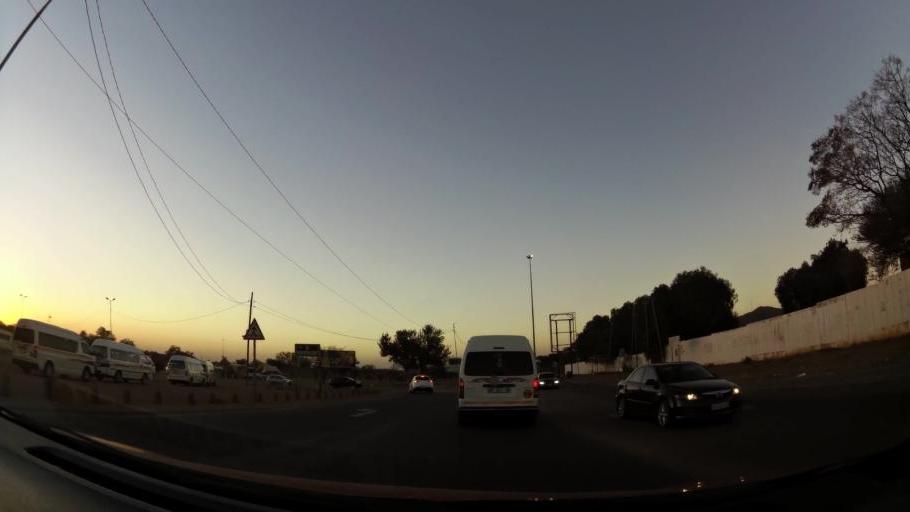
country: ZA
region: North-West
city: Ga-Rankuwa
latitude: -25.6194
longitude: 28.0069
